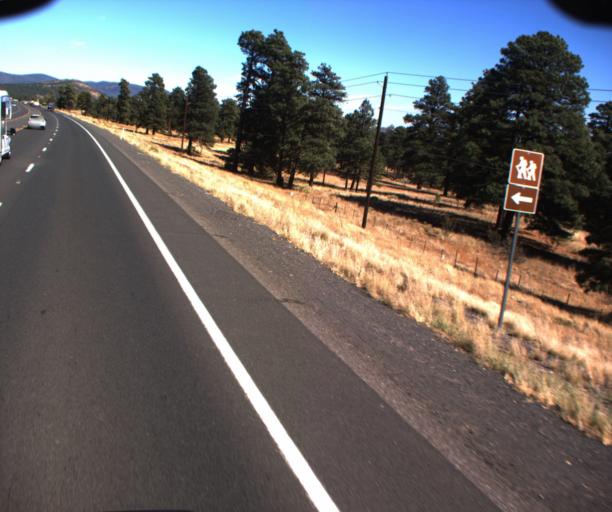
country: US
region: Arizona
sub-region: Coconino County
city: Flagstaff
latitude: 35.2480
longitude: -111.5617
